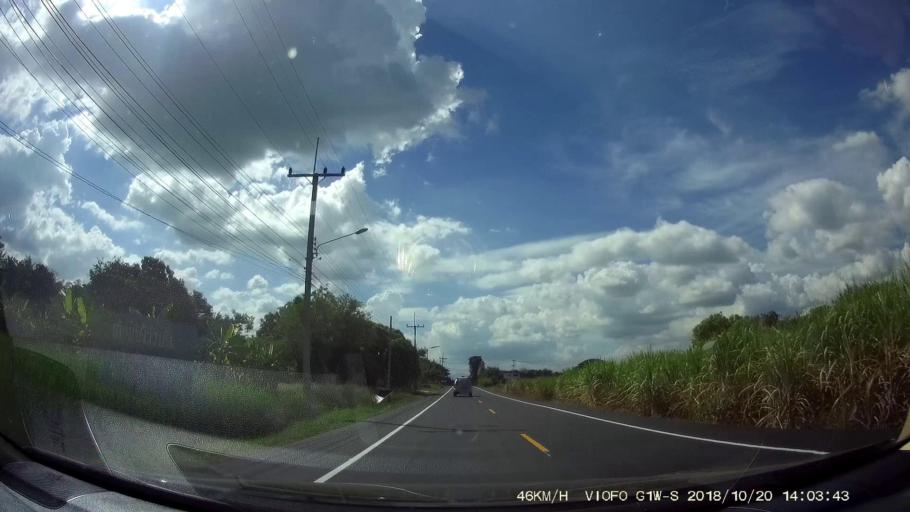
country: TH
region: Khon Kaen
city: Chum Phae
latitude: 16.4884
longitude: 102.1231
